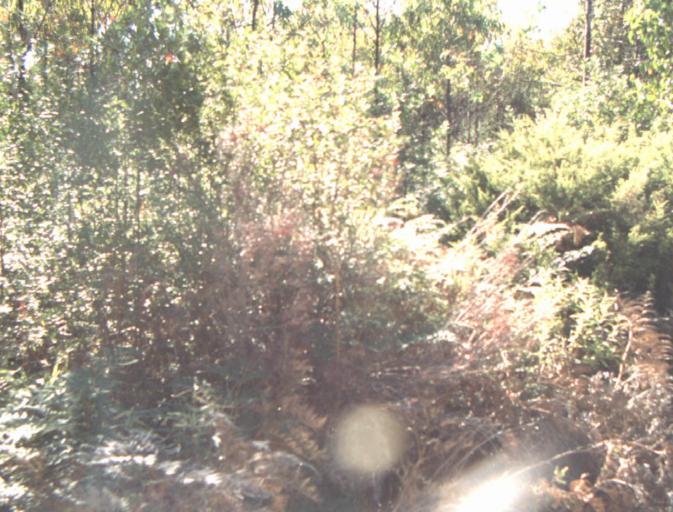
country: AU
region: Tasmania
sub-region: Dorset
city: Scottsdale
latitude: -41.3012
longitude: 147.3566
